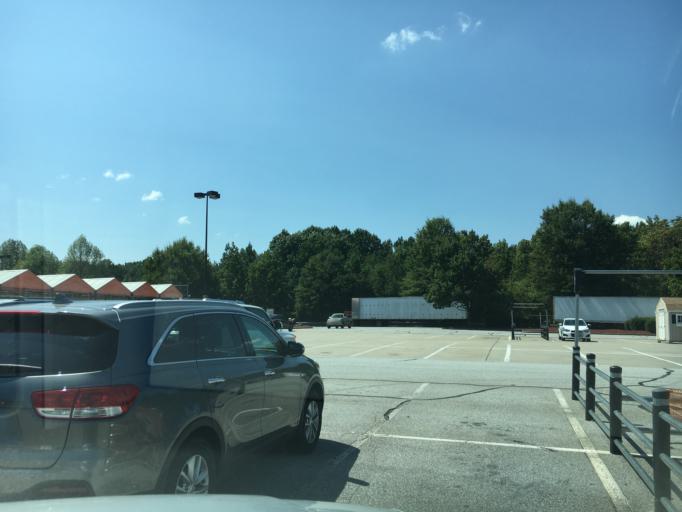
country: US
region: South Carolina
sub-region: Greenville County
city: Mauldin
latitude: 34.8284
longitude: -82.3081
